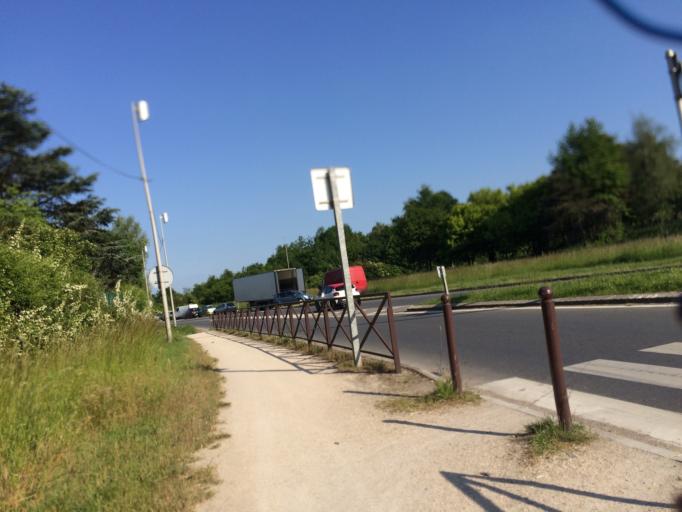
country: FR
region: Ile-de-France
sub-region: Departement de l'Essonne
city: Bondoufle
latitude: 48.6258
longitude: 2.3891
